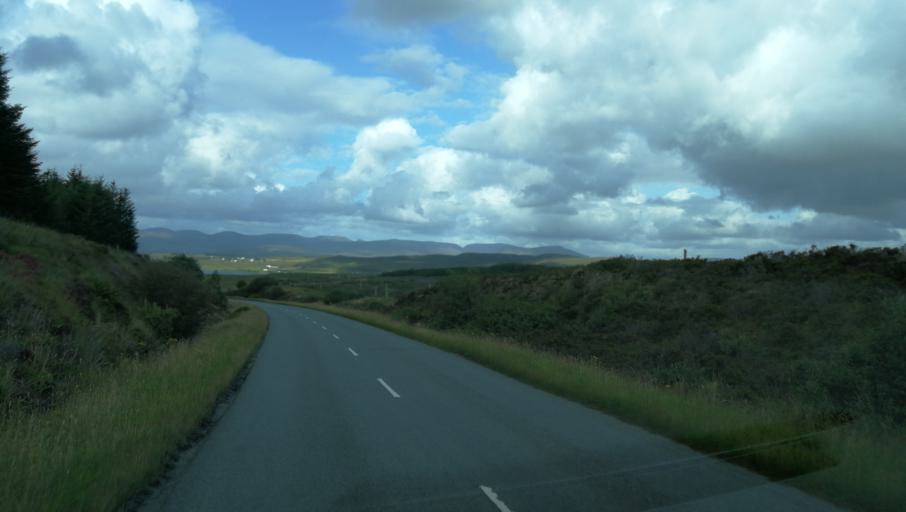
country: GB
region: Scotland
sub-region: Highland
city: Isle of Skye
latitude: 57.4667
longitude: -6.4806
